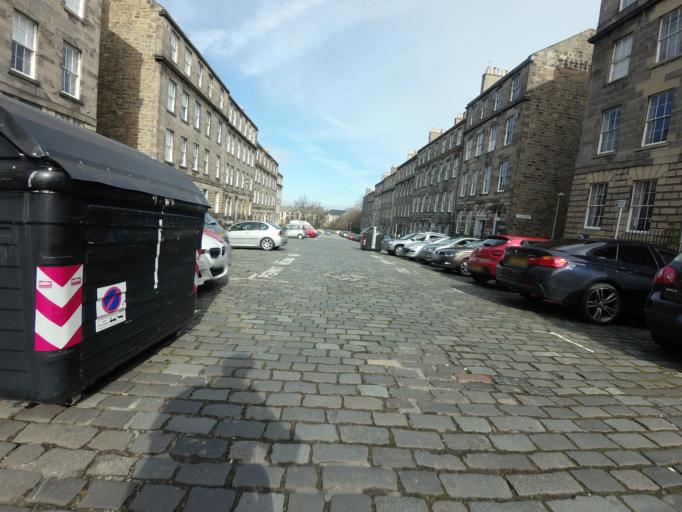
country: GB
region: Scotland
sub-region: Edinburgh
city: Edinburgh
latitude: 55.9594
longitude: -3.1949
